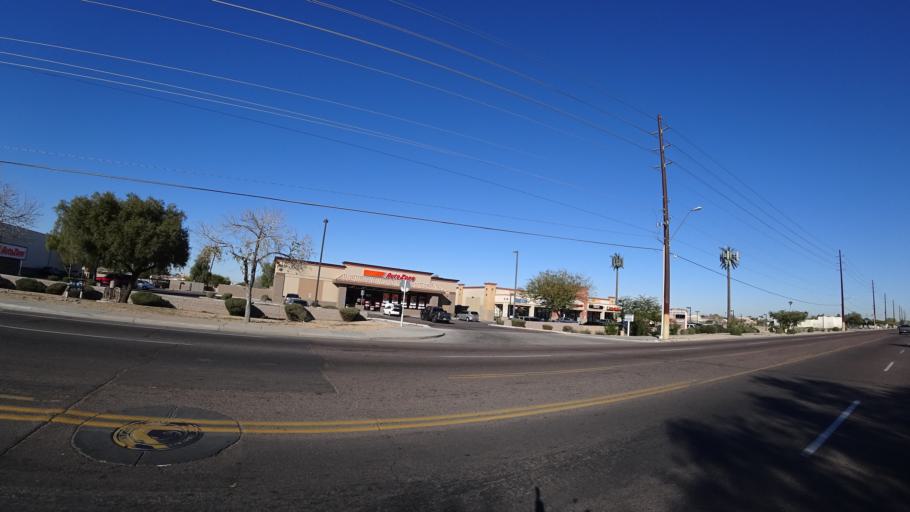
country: US
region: Arizona
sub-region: Maricopa County
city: Phoenix
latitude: 33.3922
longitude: -112.0979
